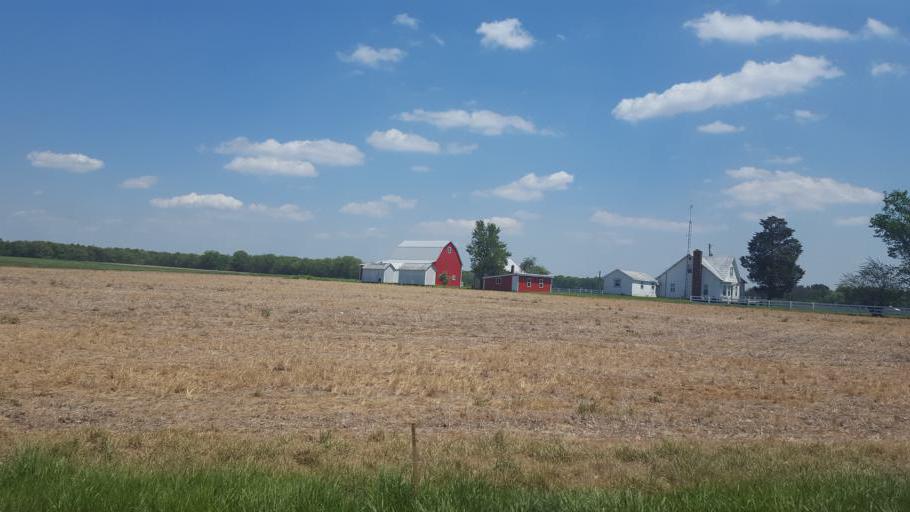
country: US
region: Ohio
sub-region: Knox County
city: Gambier
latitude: 40.3555
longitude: -82.4471
